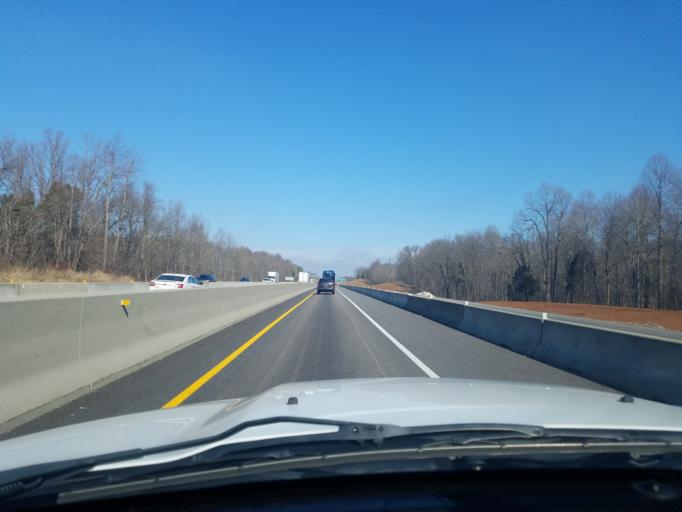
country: US
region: Kentucky
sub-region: Hardin County
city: Elizabethtown
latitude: 37.6417
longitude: -85.8587
